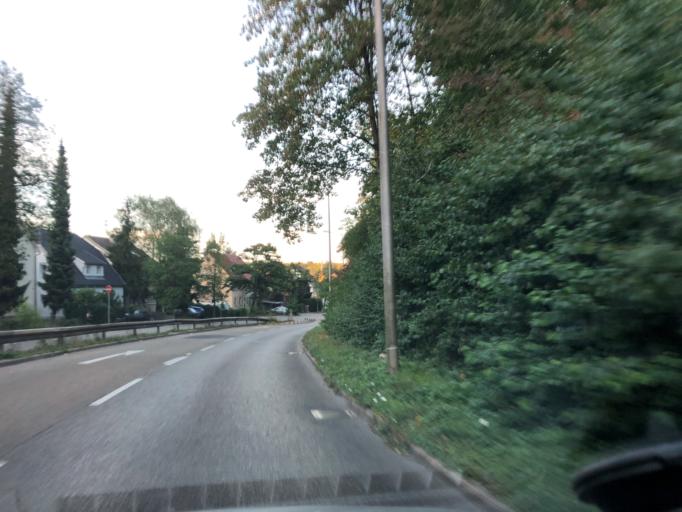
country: DE
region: Baden-Wuerttemberg
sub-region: Regierungsbezirk Stuttgart
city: Ludwigsburg
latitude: 48.9060
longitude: 9.2144
